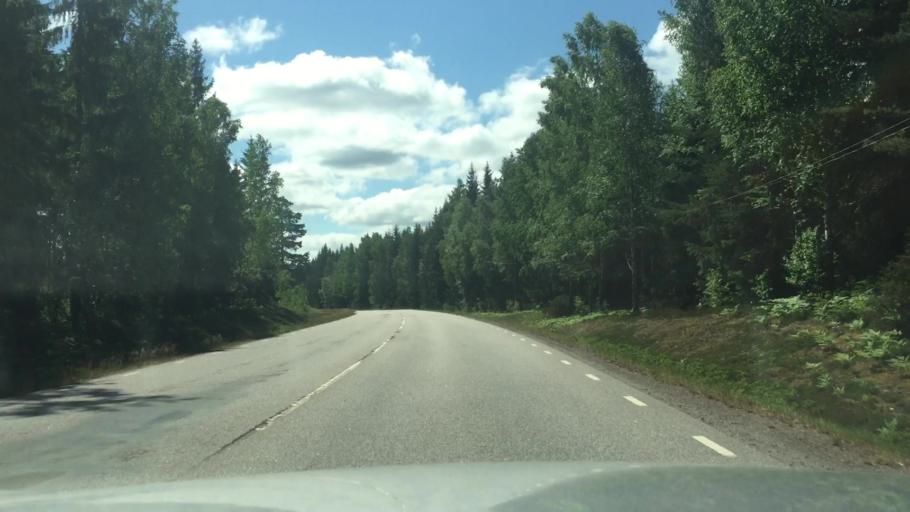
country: SE
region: Vaestra Goetaland
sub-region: Karlsborgs Kommun
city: Molltorp
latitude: 58.6210
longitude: 14.3880
